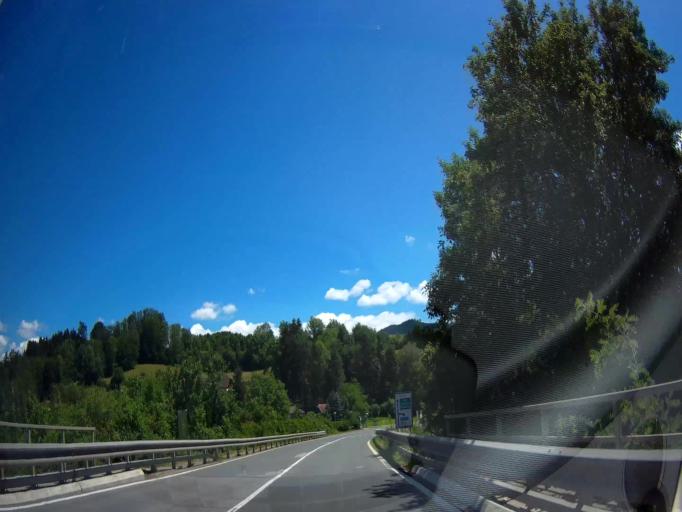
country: AT
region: Carinthia
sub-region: Politischer Bezirk Sankt Veit an der Glan
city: Sankt Veit an der Glan
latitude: 46.7459
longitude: 14.3875
